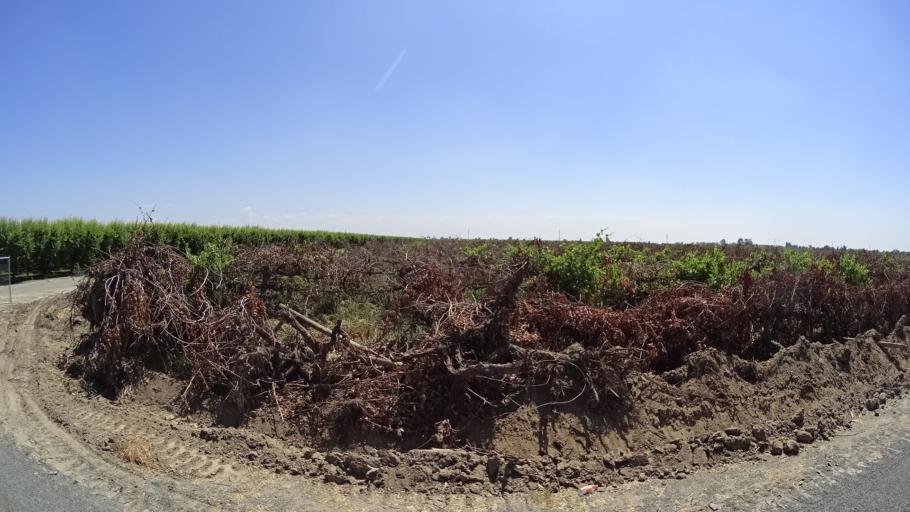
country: US
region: California
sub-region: Fresno County
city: Kingsburg
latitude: 36.4676
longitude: -119.6002
